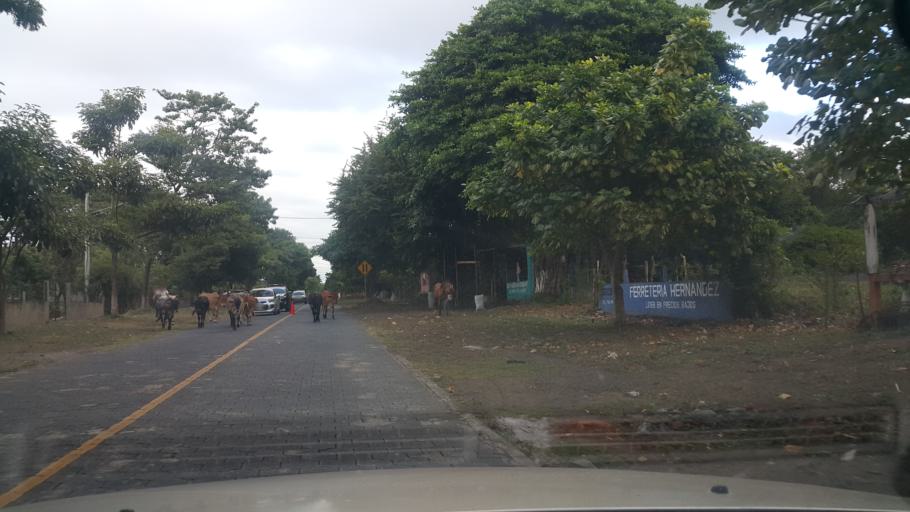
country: NI
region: Rivas
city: Moyogalpa
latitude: 11.5308
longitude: -85.6991
